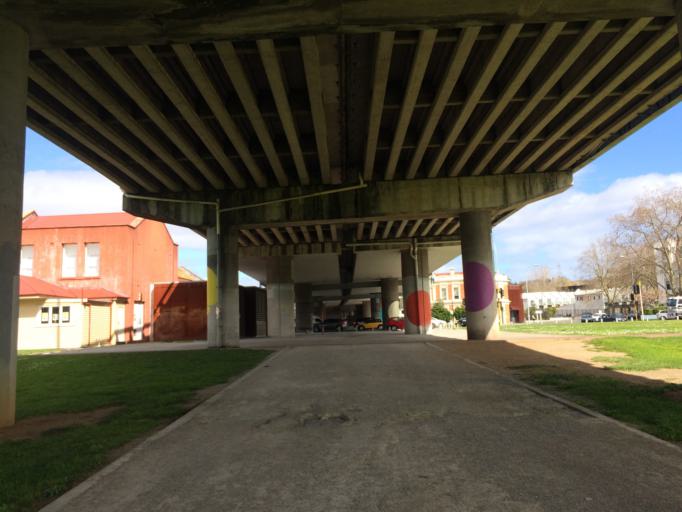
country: NZ
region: Auckland
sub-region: Auckland
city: Auckland
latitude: -36.8475
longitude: 174.7532
